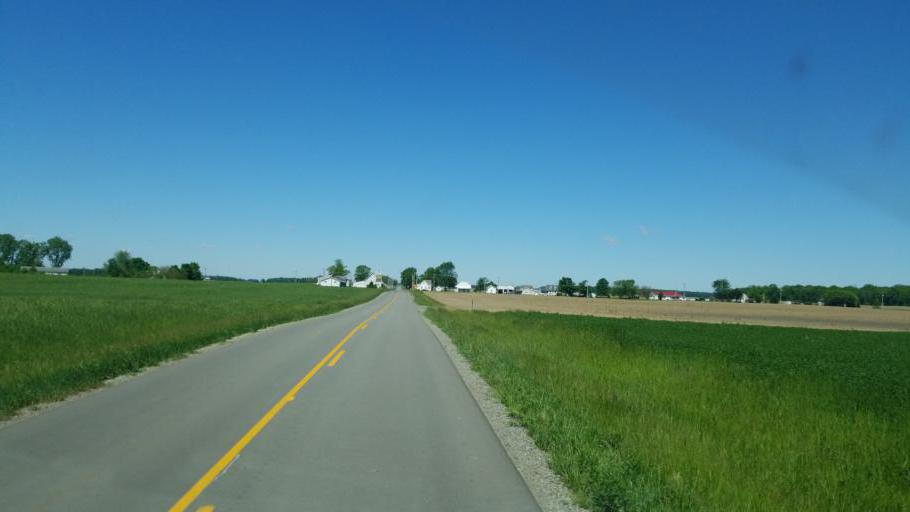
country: US
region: Ohio
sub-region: Logan County
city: Lakeview
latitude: 40.4174
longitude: -83.9405
